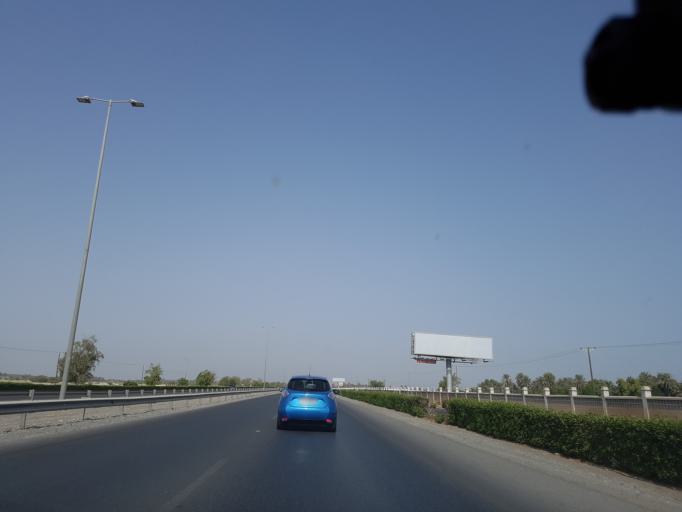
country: OM
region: Al Batinah
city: Barka'
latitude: 23.7357
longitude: 57.6729
